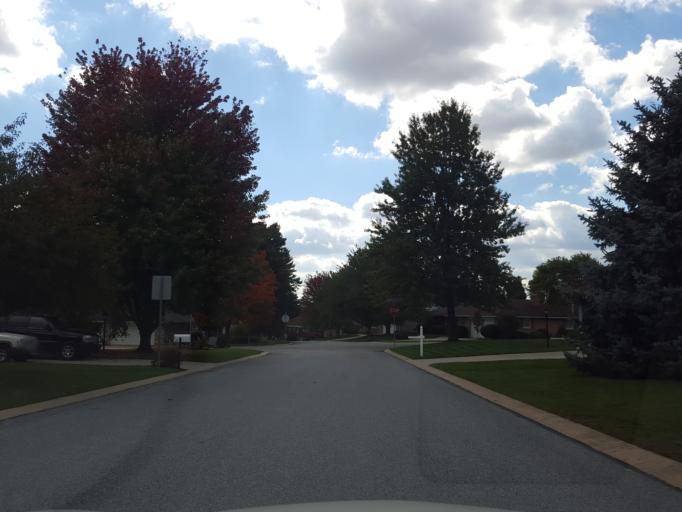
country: US
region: Pennsylvania
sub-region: York County
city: East York
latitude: 39.9542
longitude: -76.6651
